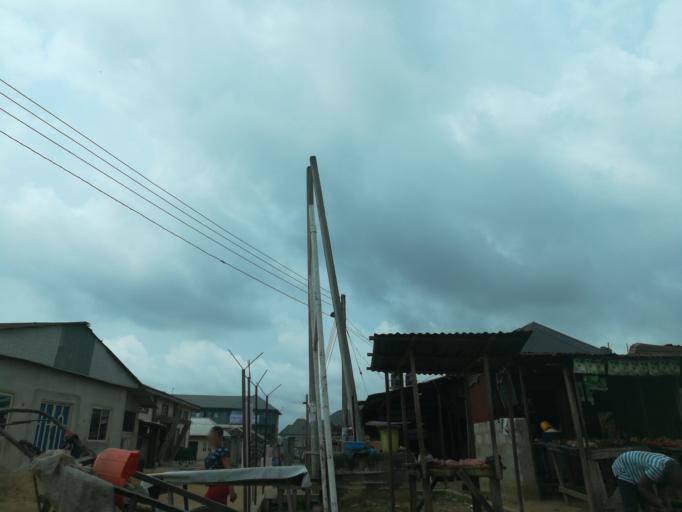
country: NG
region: Rivers
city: Emuoha
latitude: 4.9060
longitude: 6.9868
